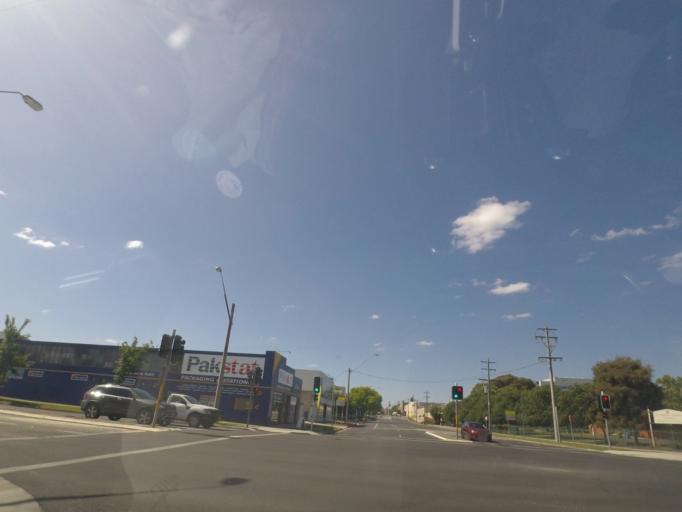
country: AU
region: New South Wales
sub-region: Albury Municipality
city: South Albury
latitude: -36.0850
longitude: 146.9148
